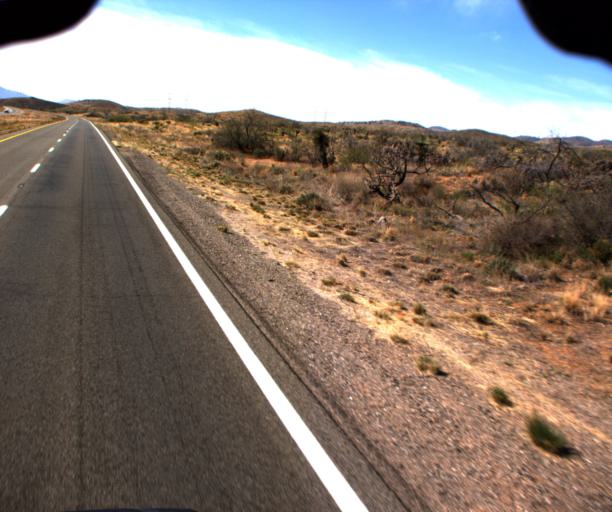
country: US
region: Arizona
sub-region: Graham County
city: Swift Trail Junction
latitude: 32.4786
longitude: -109.6732
